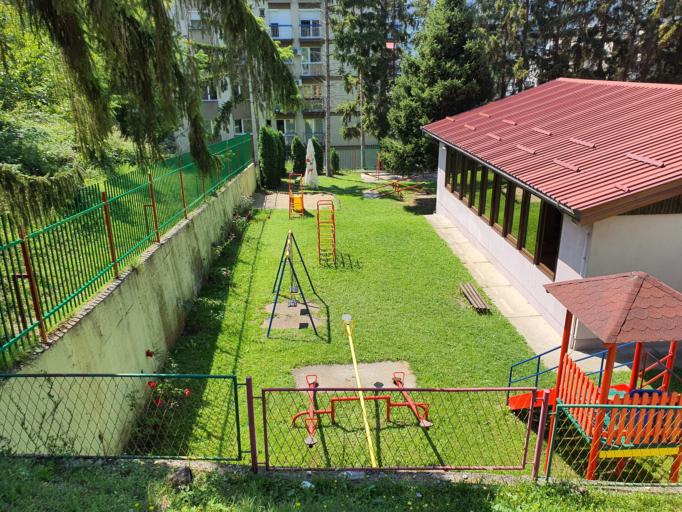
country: RS
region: Central Serbia
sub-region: Zlatiborski Okrug
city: Uzice
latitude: 43.8534
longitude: 19.8600
